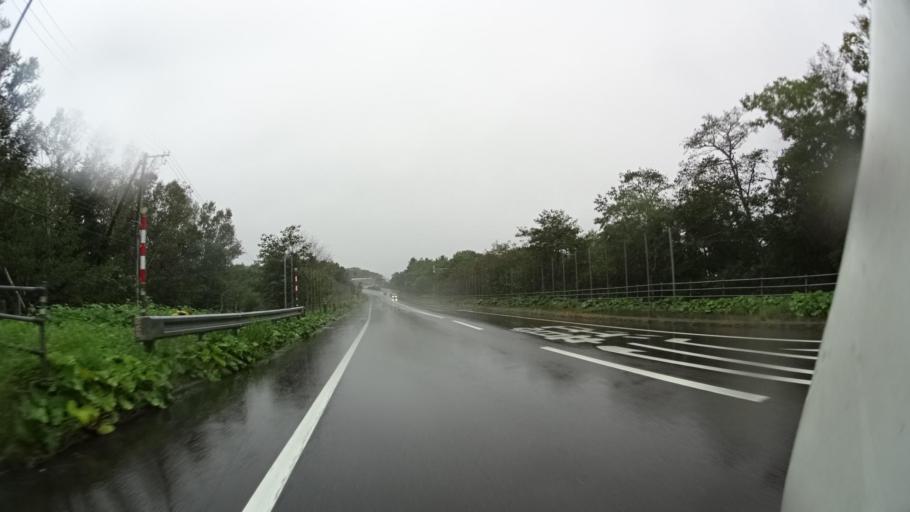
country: JP
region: Hokkaido
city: Nemuro
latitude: 43.2597
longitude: 145.4428
